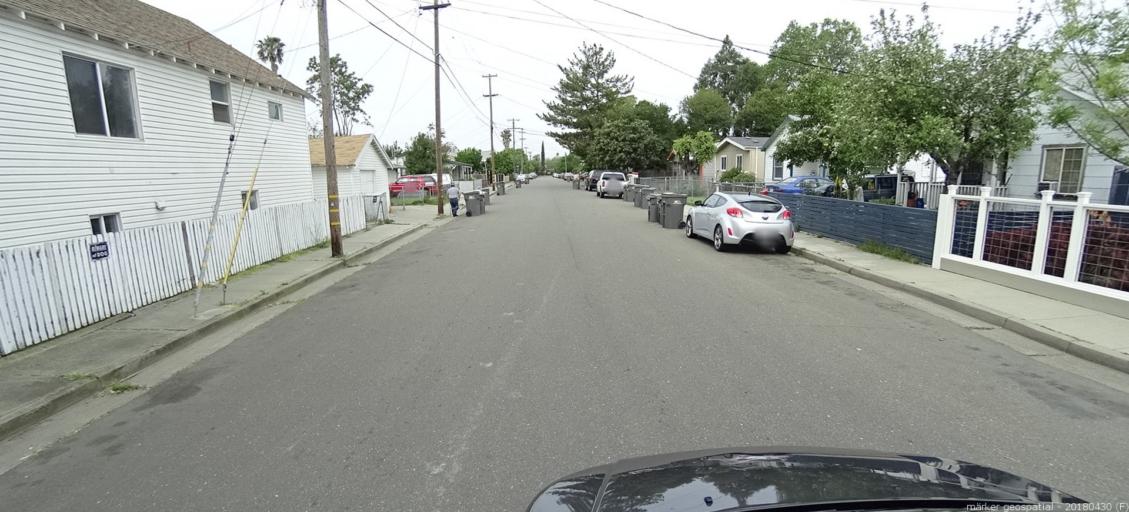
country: US
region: California
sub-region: Yolo County
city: West Sacramento
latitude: 38.5900
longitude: -121.5142
